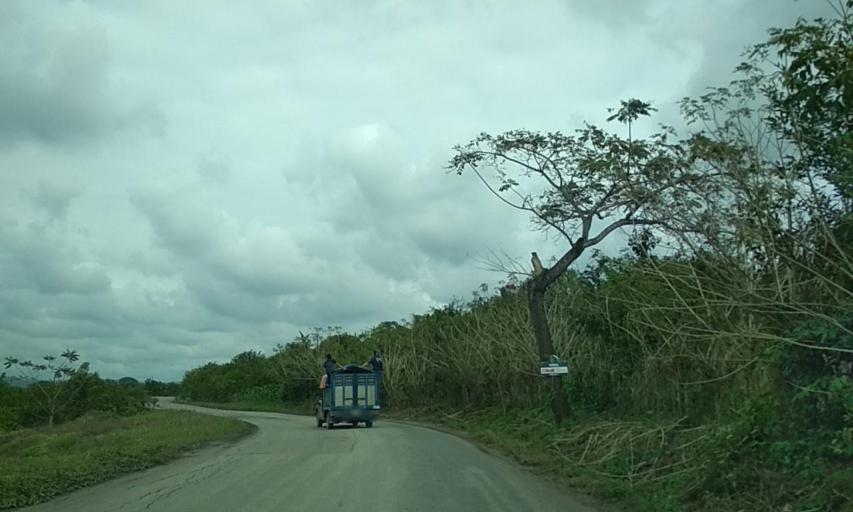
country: MX
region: Veracruz
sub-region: Papantla
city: El Chote
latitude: 20.3519
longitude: -97.3528
